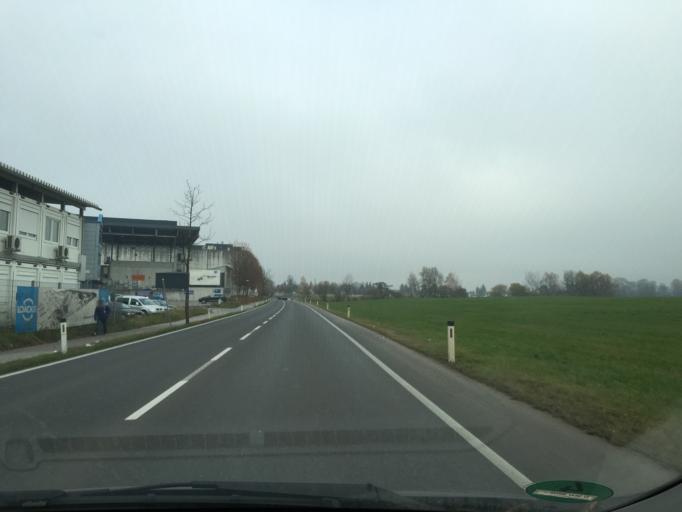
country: AT
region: Vorarlberg
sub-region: Politischer Bezirk Feldkirch
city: Altach
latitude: 47.3480
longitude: 9.6581
